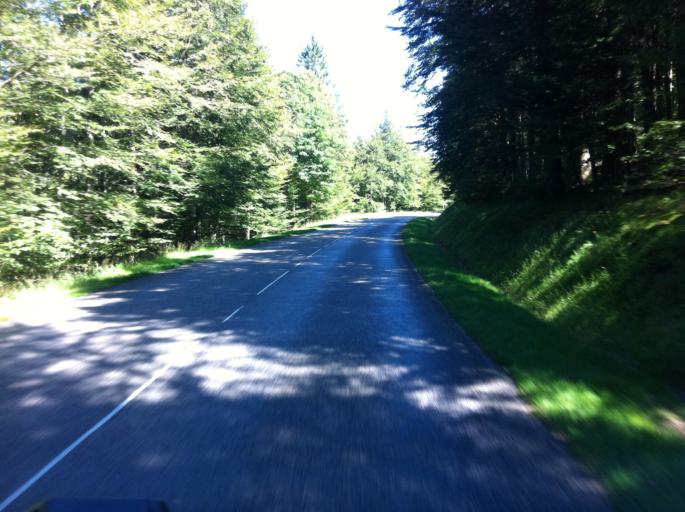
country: FR
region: Alsace
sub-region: Departement du Haut-Rhin
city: Metzeral
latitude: 48.0724
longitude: 7.0216
